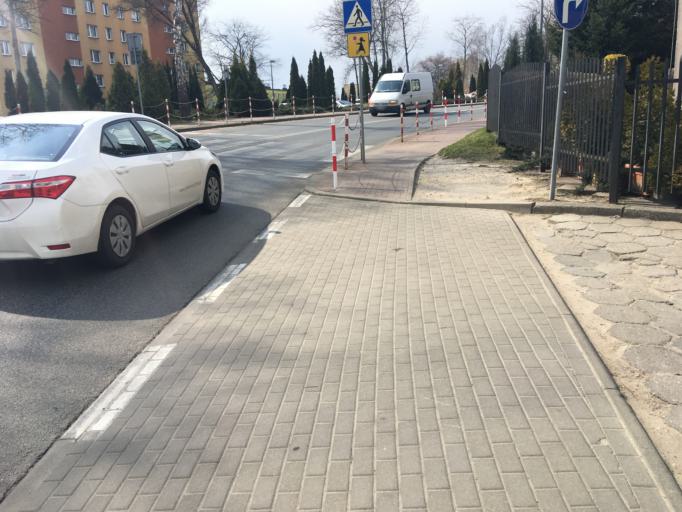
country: PL
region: Swietokrzyskie
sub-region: Powiat starachowicki
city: Starachowice
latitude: 51.0542
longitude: 21.0636
